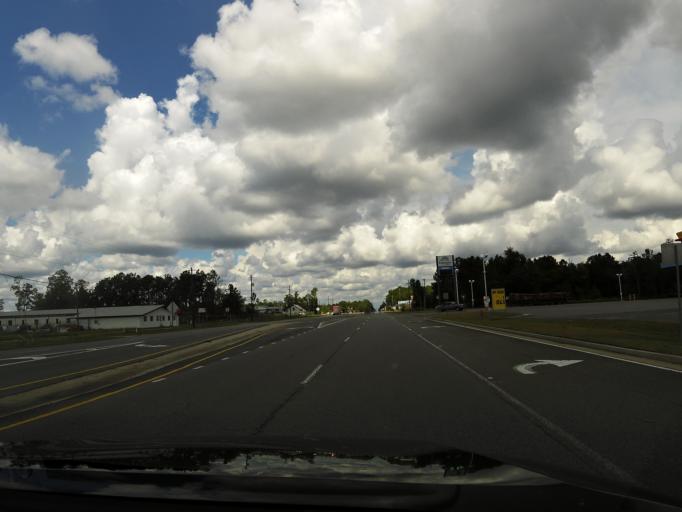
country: US
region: Georgia
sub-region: Charlton County
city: Folkston
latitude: 30.8578
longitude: -82.0105
